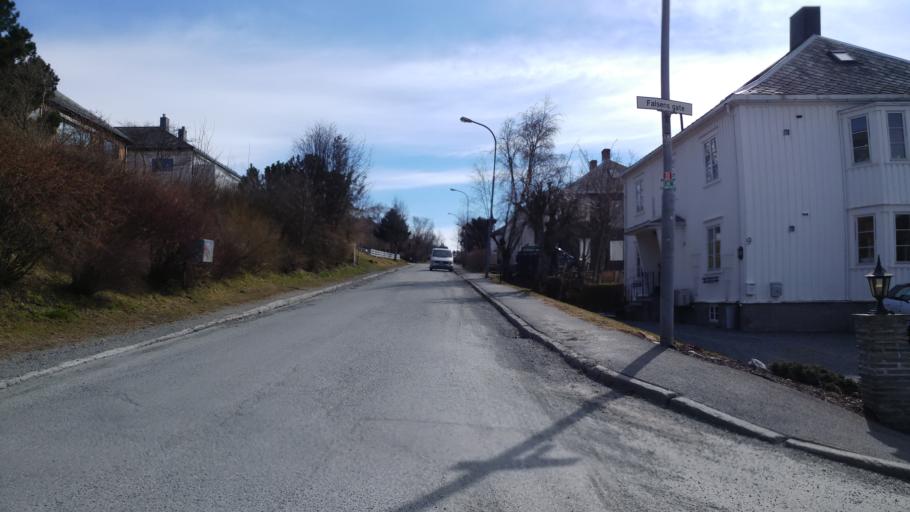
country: NO
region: Sor-Trondelag
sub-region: Trondheim
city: Trondheim
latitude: 63.4262
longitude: 10.4219
